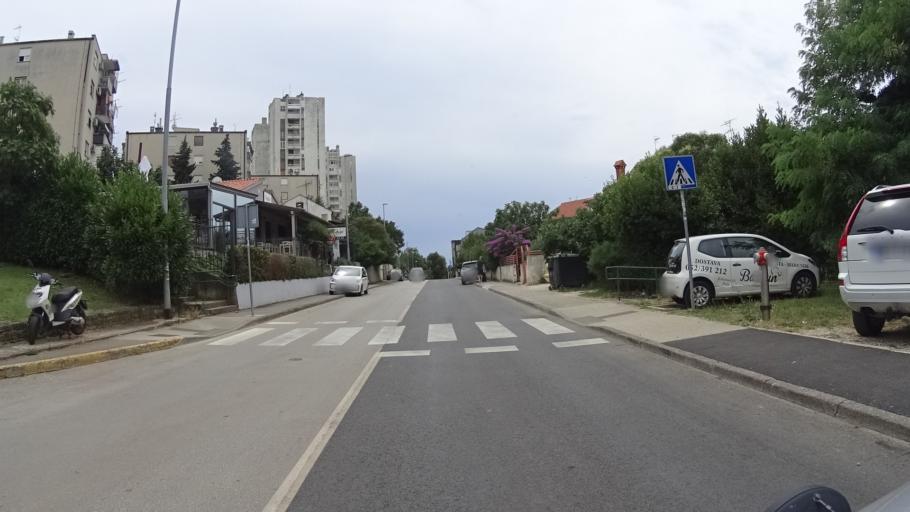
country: HR
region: Istarska
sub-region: Grad Pula
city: Pula
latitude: 44.8553
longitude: 13.8424
